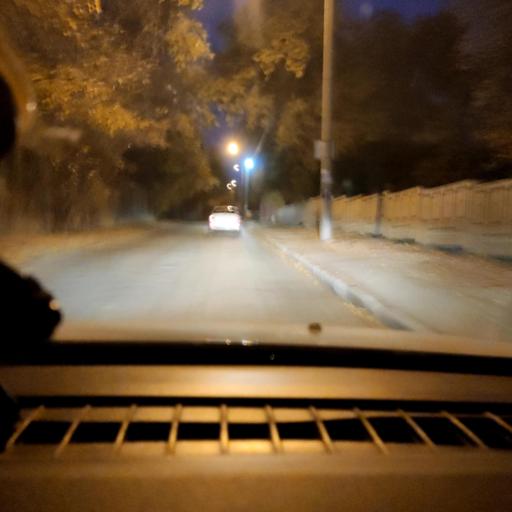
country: RU
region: Samara
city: Samara
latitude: 53.1920
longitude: 50.1561
